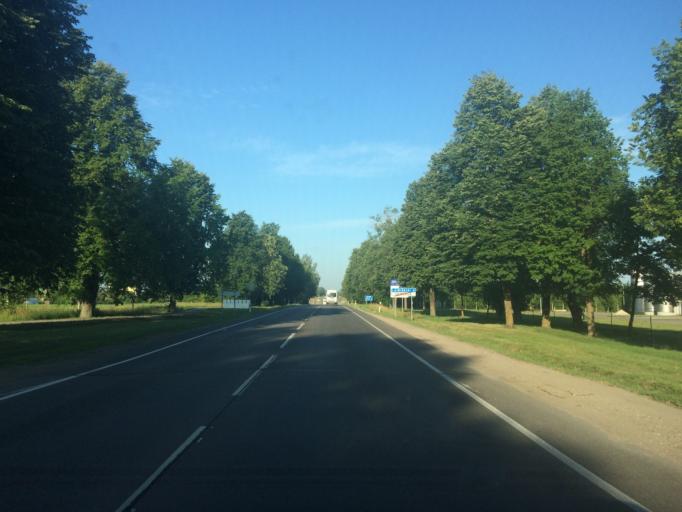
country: LT
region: Vilnius County
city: Ukmerge
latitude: 55.2374
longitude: 24.7299
